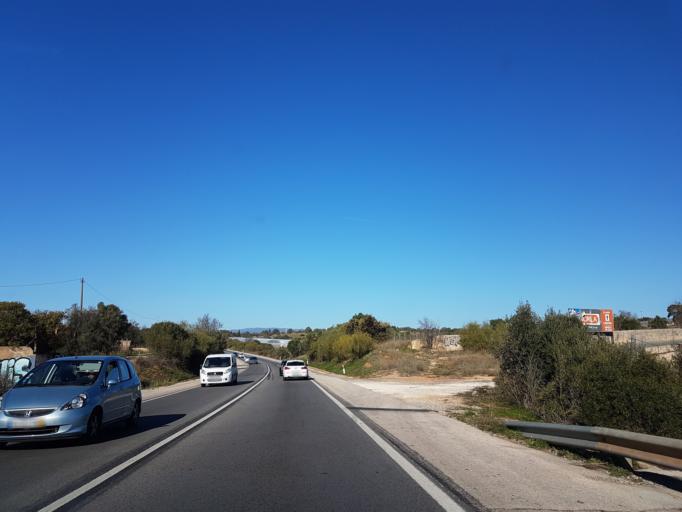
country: PT
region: Faro
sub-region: Lagoa
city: Estombar
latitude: 37.1479
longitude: -8.4788
